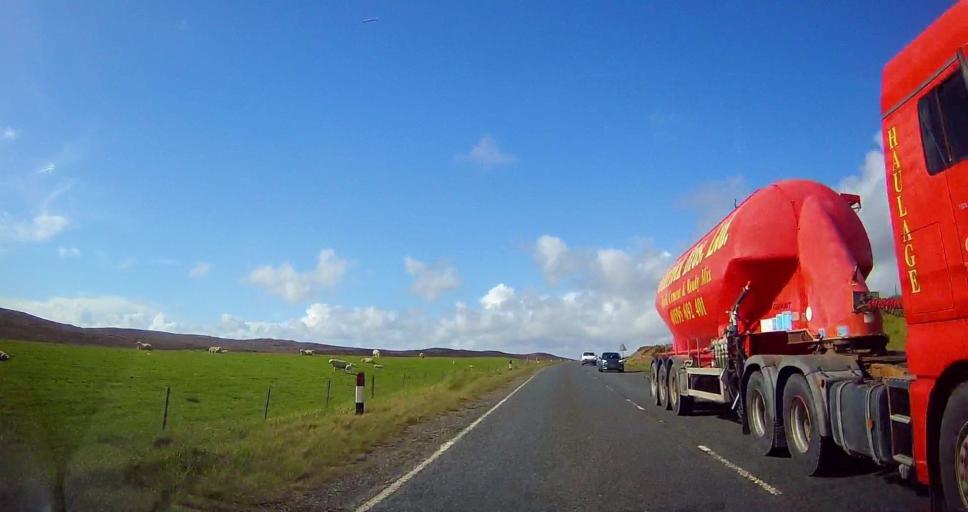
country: GB
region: Scotland
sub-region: Shetland Islands
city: Lerwick
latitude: 60.1991
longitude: -1.2325
